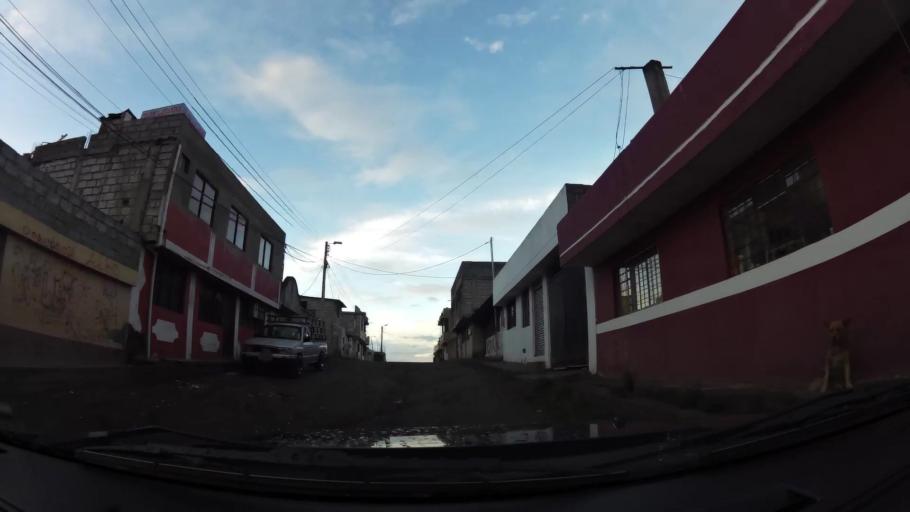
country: EC
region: Pichincha
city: Quito
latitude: -0.0966
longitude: -78.5172
